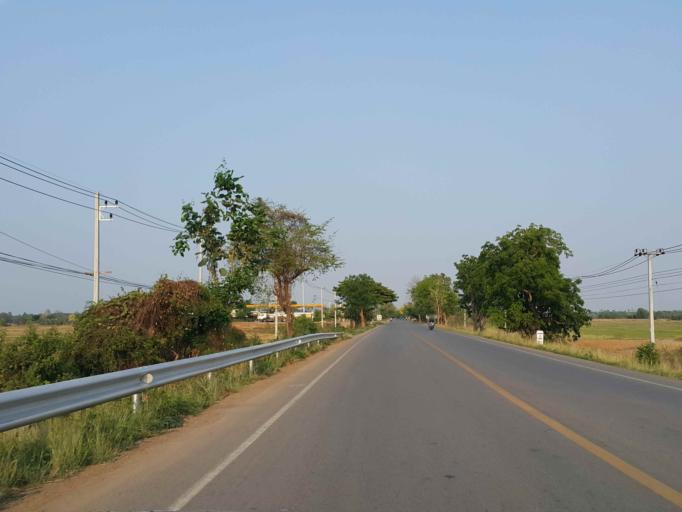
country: TH
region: Sukhothai
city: Sawankhalok
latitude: 17.3104
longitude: 99.8016
